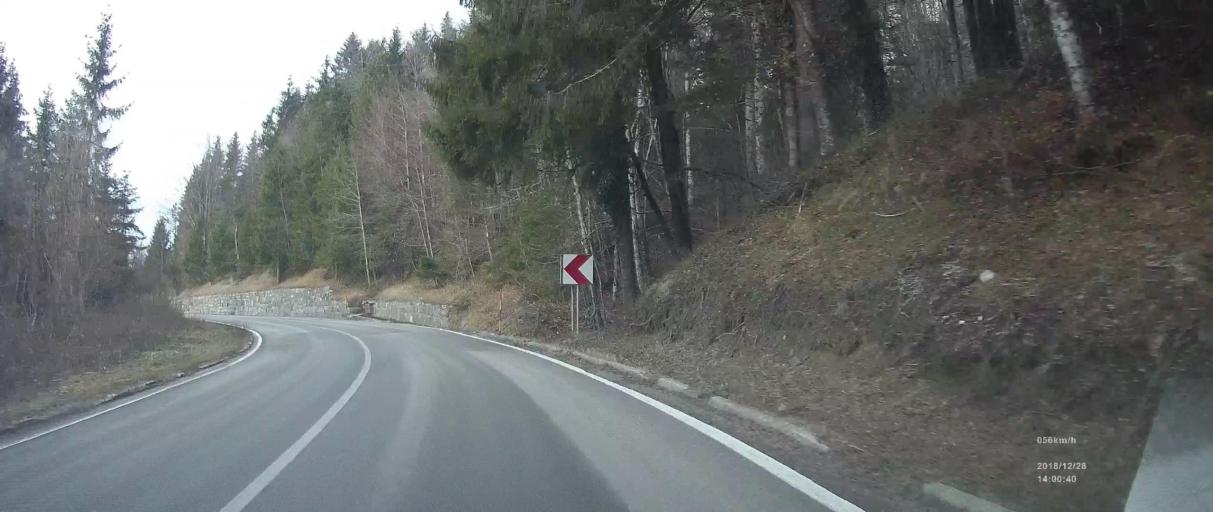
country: SI
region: Kostel
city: Kostel
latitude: 45.4140
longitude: 14.9141
